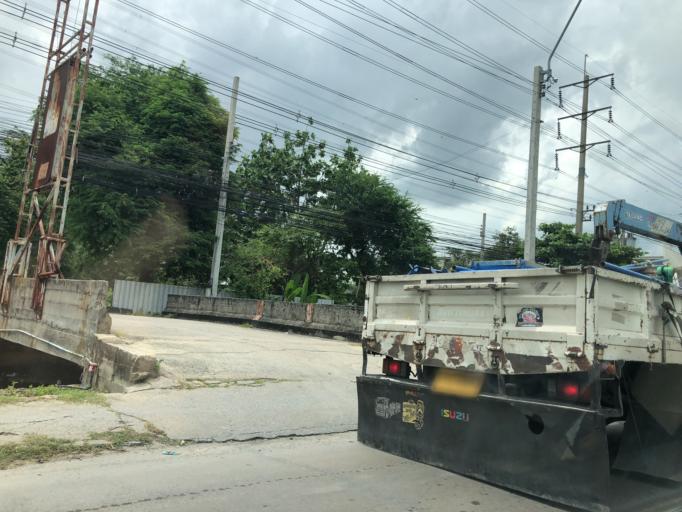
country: TH
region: Bangkok
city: Lak Si
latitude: 13.8840
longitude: 100.5519
